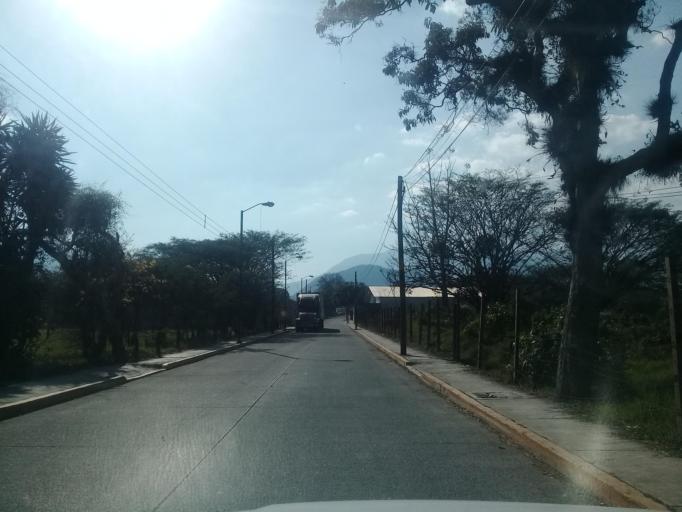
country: MX
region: Veracruz
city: Jalapilla
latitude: 18.8427
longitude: -97.0778
